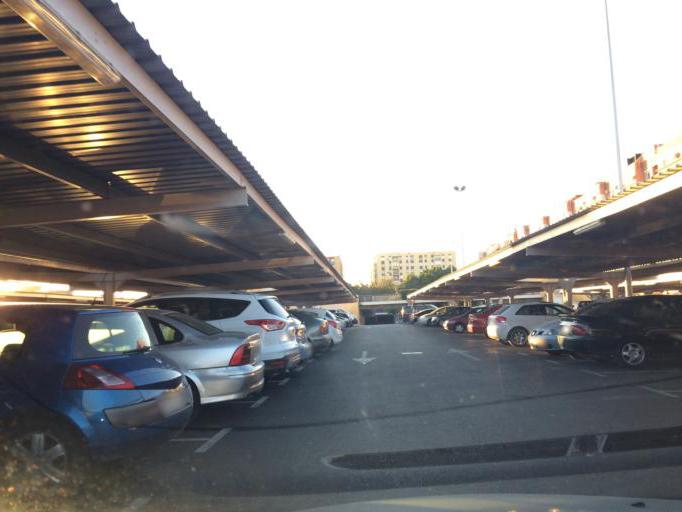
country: ES
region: Andalusia
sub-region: Provincia de Almeria
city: Almeria
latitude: 36.8418
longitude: -2.4445
